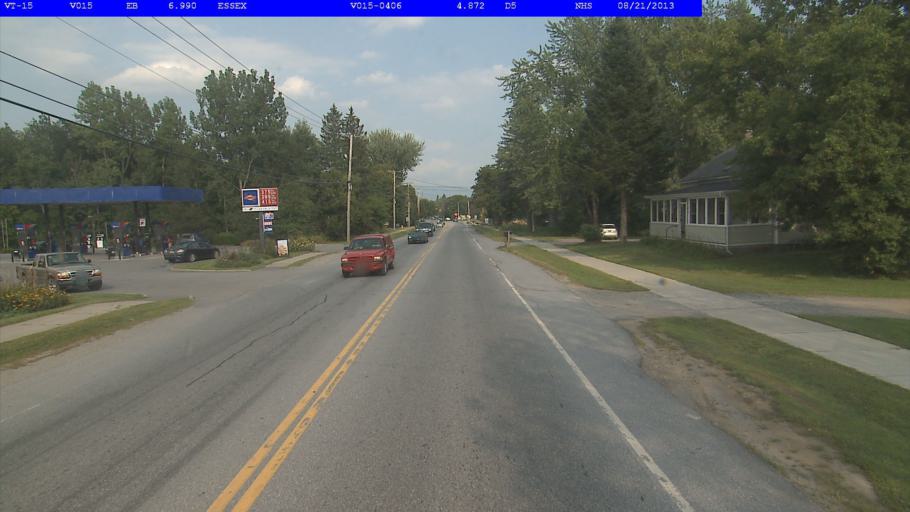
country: US
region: Vermont
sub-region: Chittenden County
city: Essex Junction
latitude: 44.5107
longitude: -73.0691
